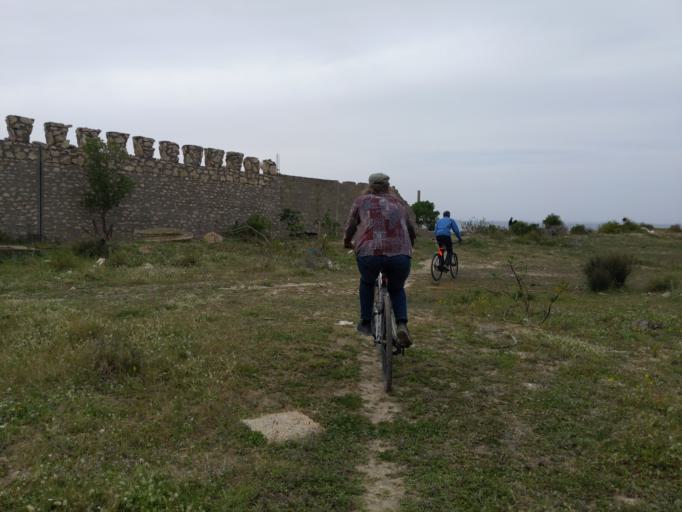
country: TN
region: Al Munastir
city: Saqanis
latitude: 35.7754
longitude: 10.7776
